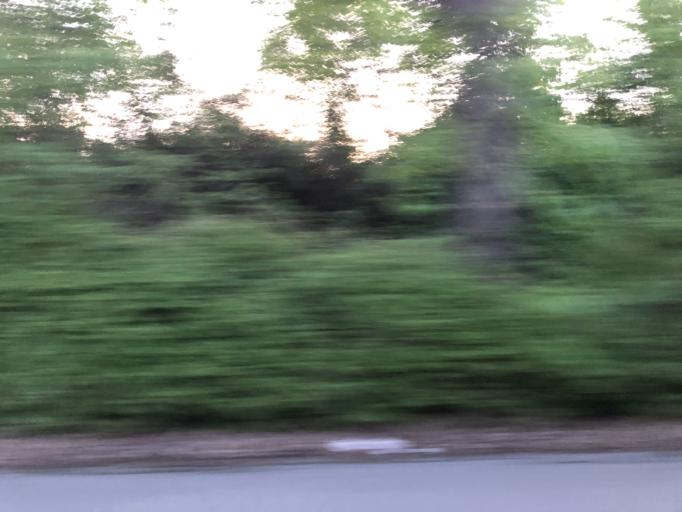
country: DE
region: Baden-Wuerttemberg
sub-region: Tuebingen Region
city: Sickenhausen
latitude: 48.5256
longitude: 9.2039
